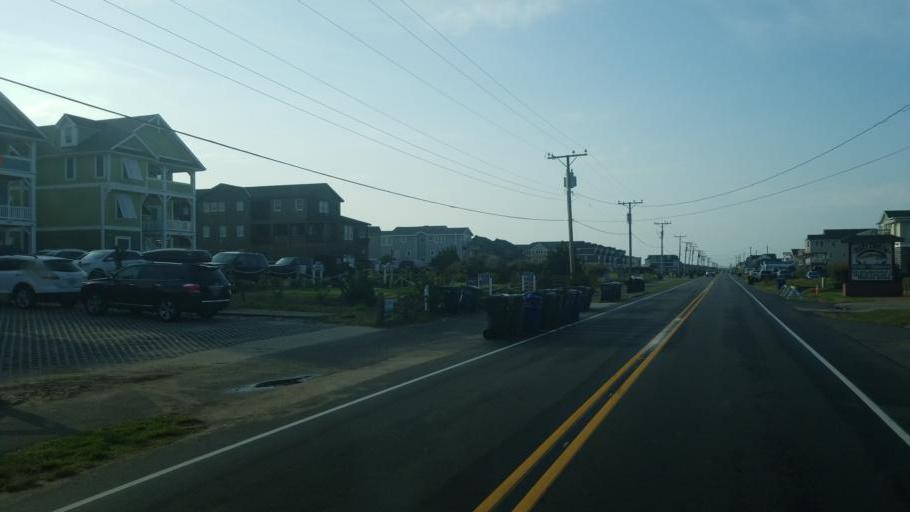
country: US
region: North Carolina
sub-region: Dare County
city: Nags Head
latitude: 35.9888
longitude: -75.6422
